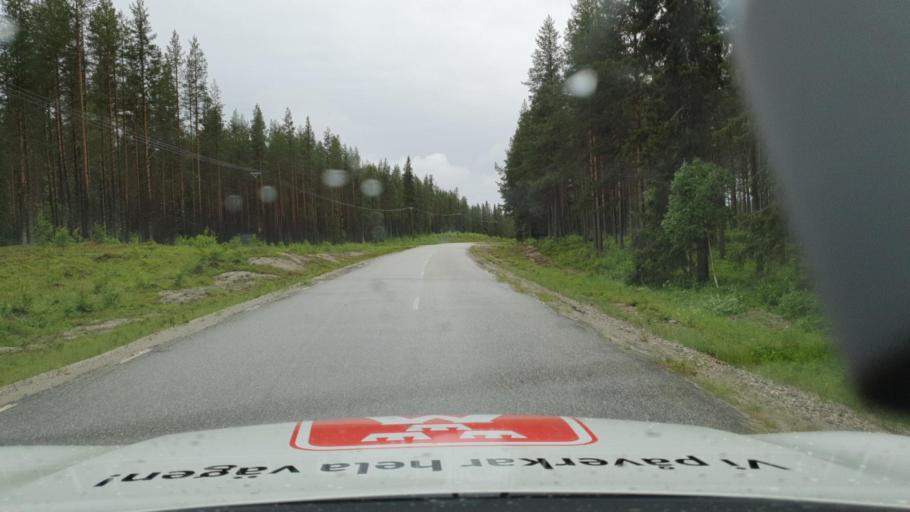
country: SE
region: Vaesterbotten
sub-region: Asele Kommun
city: Asele
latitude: 63.9883
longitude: 17.1678
